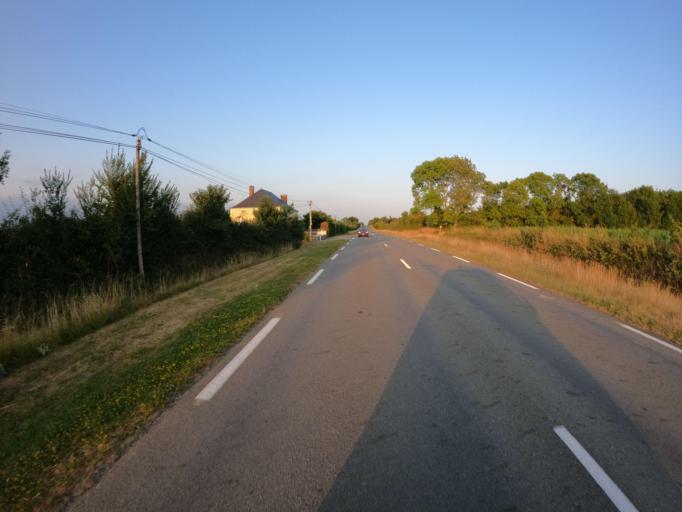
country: FR
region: Pays de la Loire
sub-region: Departement de la Mayenne
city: Meslay-du-Maine
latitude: 47.8710
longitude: -0.4798
